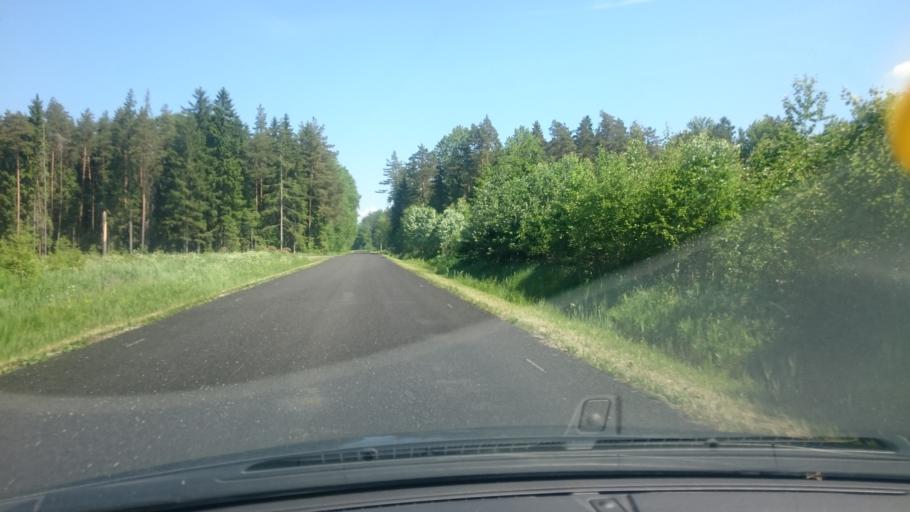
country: EE
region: Harju
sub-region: Rae vald
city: Vaida
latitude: 59.2301
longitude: 25.0133
